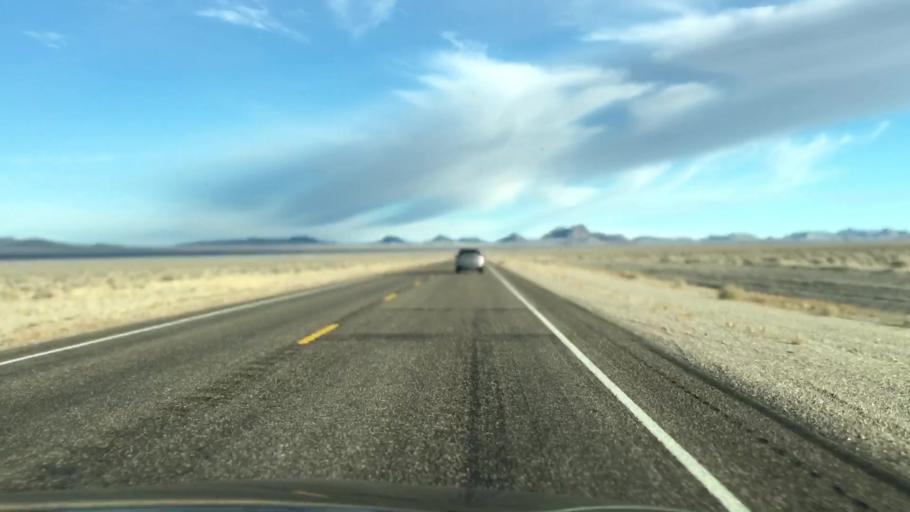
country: US
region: Nevada
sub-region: Nye County
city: Tonopah
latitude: 38.1250
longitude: -117.4069
